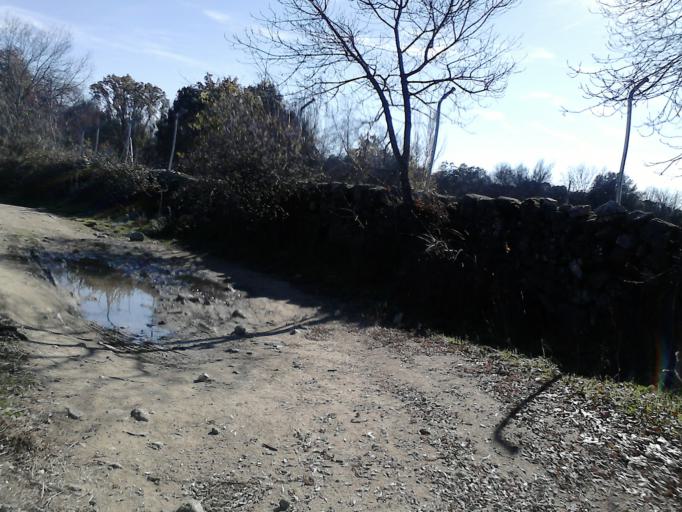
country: ES
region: Madrid
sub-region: Provincia de Madrid
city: El Escorial
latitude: 40.6059
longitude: -4.0943
